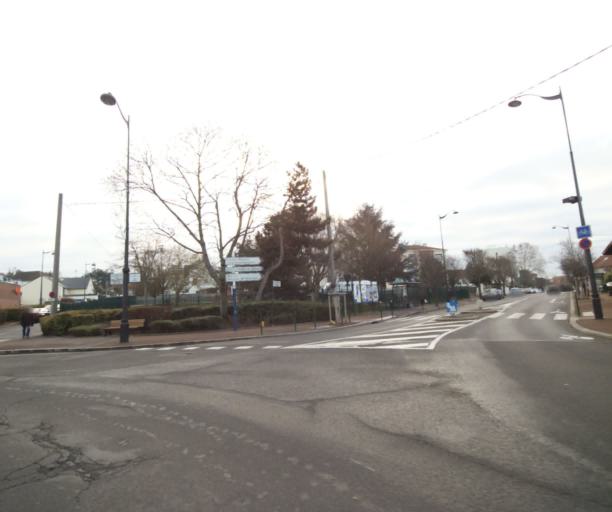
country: FR
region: Ile-de-France
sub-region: Departement des Hauts-de-Seine
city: Rueil-Malmaison
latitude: 48.8763
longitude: 2.2008
